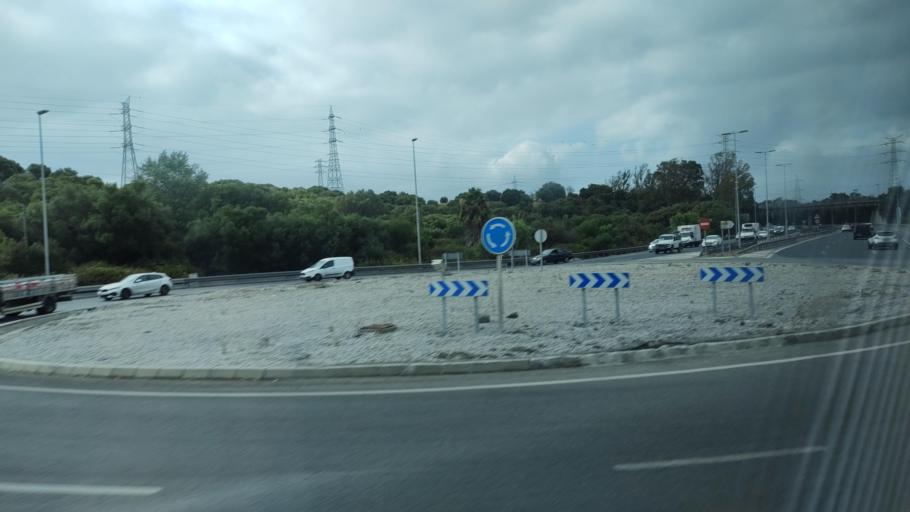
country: ES
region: Andalusia
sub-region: Provincia de Cadiz
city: San Roque
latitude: 36.1917
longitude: -5.3853
